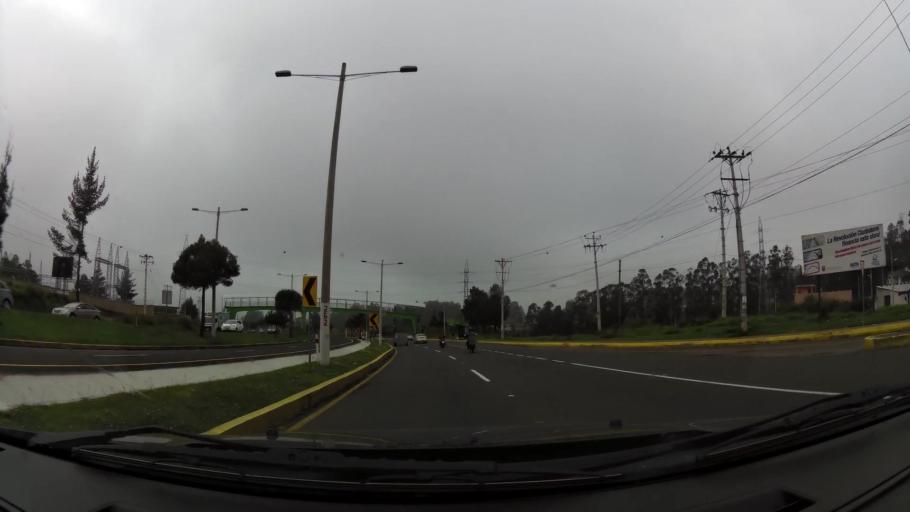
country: EC
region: Pichincha
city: Quito
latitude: -0.2754
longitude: -78.4899
